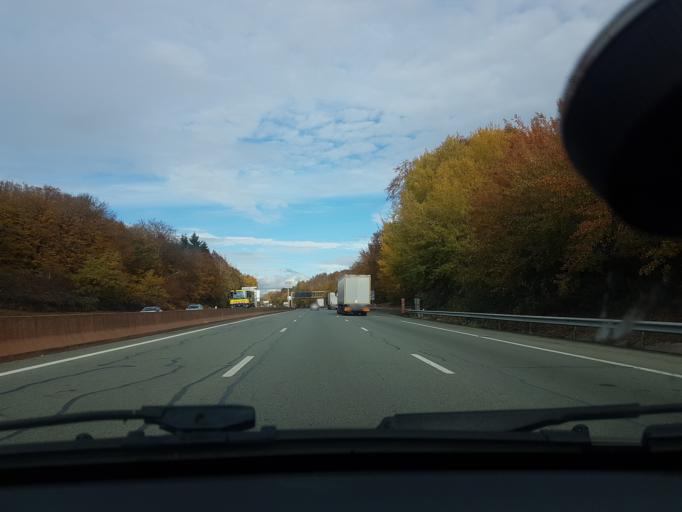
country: FR
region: Franche-Comte
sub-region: Territoire de Belfort
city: Andelnans
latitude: 47.6010
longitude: 6.8561
